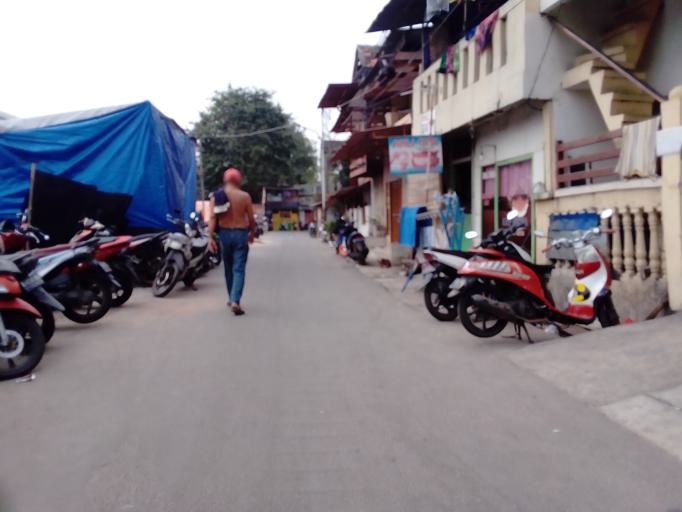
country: ID
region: Jakarta Raya
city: Jakarta
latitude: -6.1568
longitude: 106.8111
